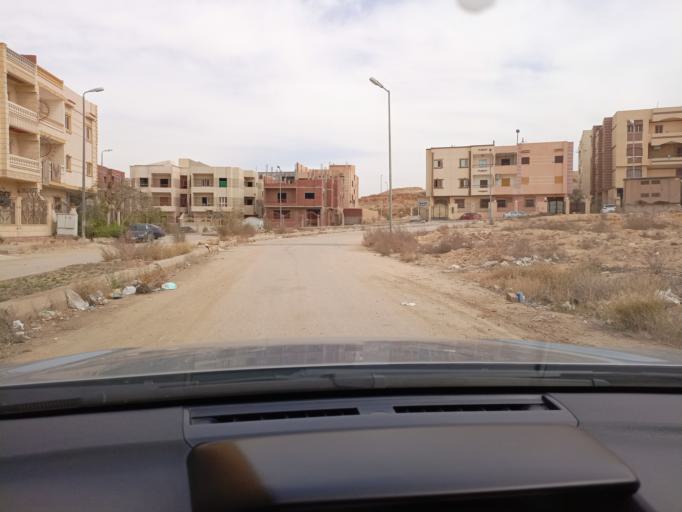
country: EG
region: Muhafazat al Qalyubiyah
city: Al Khankah
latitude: 30.2448
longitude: 31.4954
